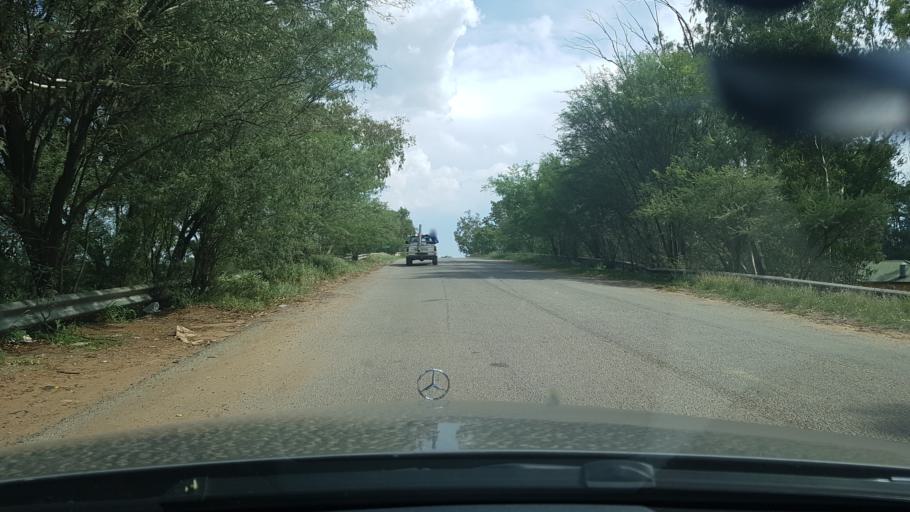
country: ZA
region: North-West
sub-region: Dr Ruth Segomotsi Mompati District Municipality
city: Bloemhof
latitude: -27.6528
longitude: 25.5960
